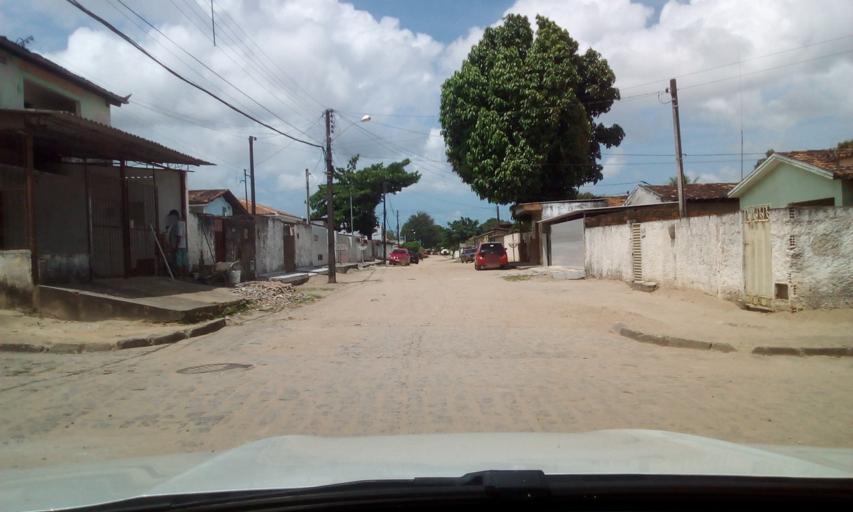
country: BR
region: Paraiba
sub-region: Bayeux
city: Bayeux
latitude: -7.1802
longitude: -34.9193
